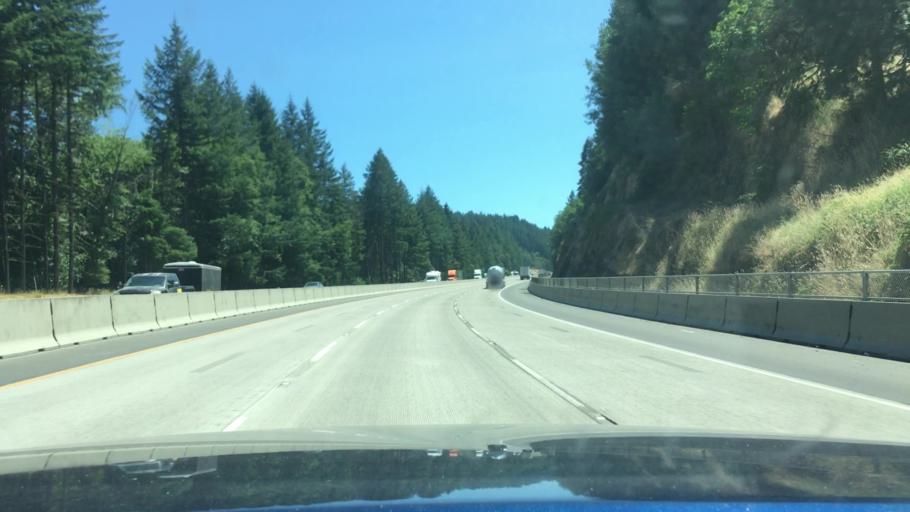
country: US
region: Oregon
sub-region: Douglas County
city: Drain
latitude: 43.7031
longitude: -123.2049
